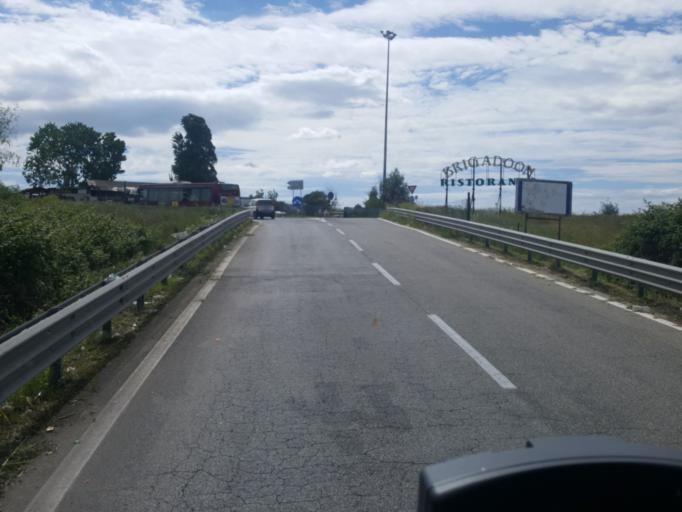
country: IT
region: Latium
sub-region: Citta metropolitana di Roma Capitale
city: La Massimina-Casal Lumbroso
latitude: 41.8878
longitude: 12.3658
